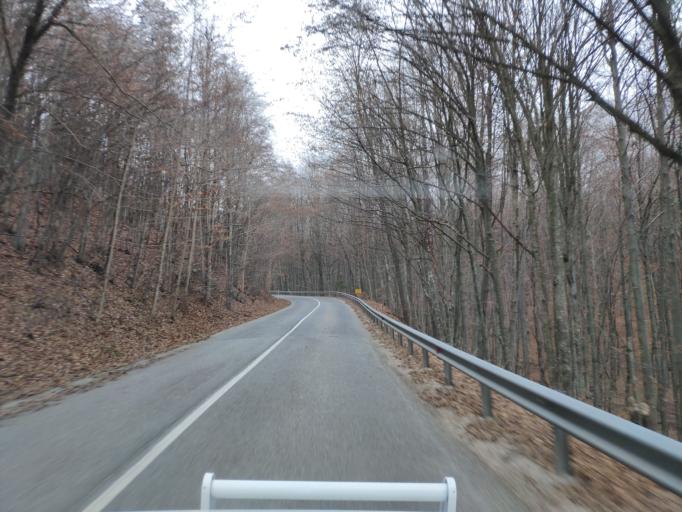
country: SK
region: Kosicky
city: Dobsina
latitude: 48.7929
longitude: 20.4783
